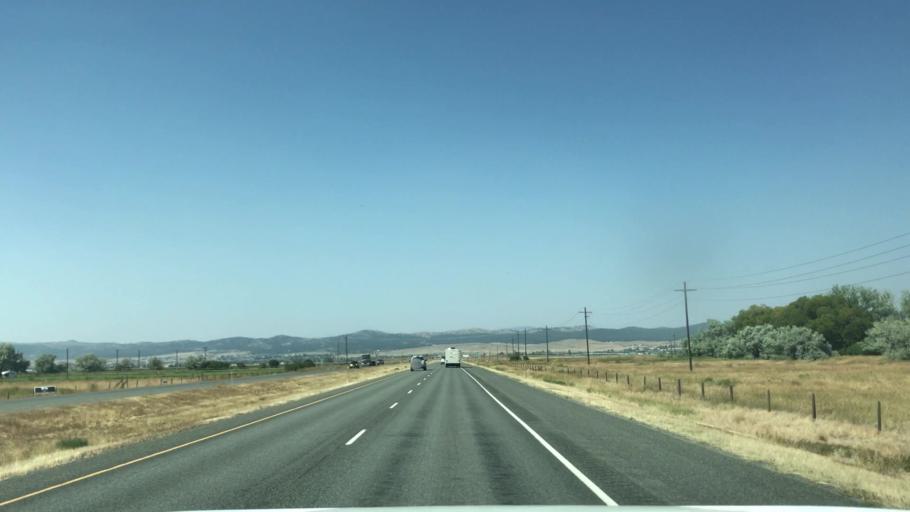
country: US
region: Montana
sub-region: Lewis and Clark County
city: Helena Valley West Central
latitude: 46.6867
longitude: -112.0116
